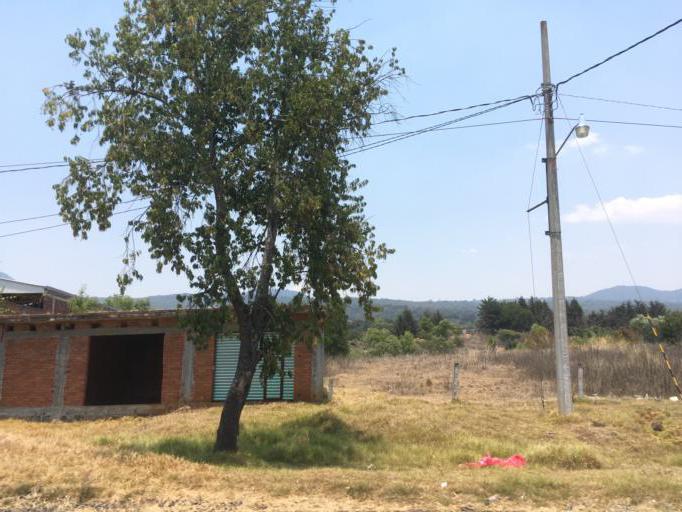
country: MX
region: Michoacan
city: Quiroga
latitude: 19.6469
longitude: -101.4919
